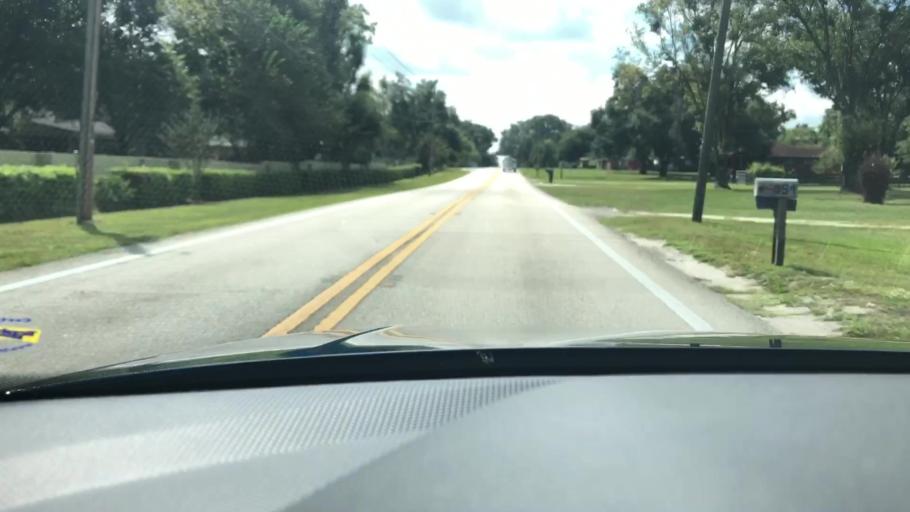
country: US
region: Florida
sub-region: Polk County
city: Gibsonia
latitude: 28.1437
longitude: -81.9384
